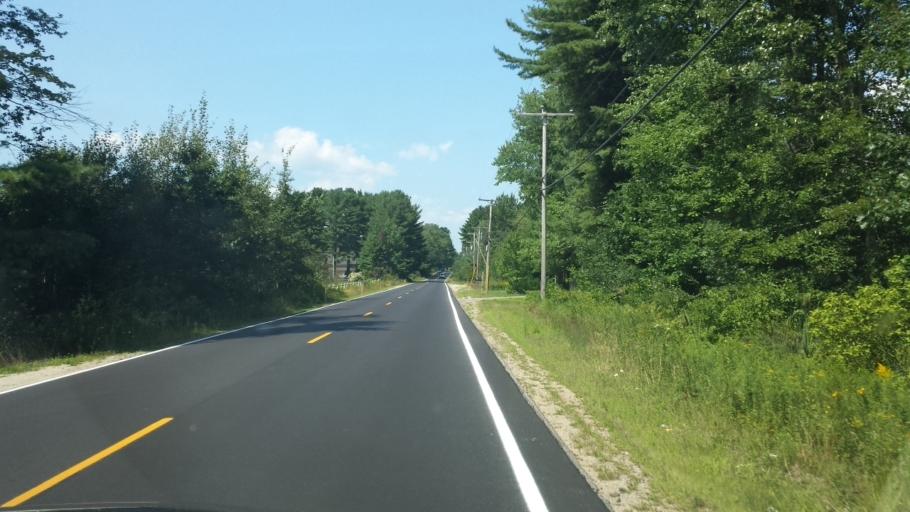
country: US
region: Maine
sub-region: York County
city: Arundel
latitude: 43.3997
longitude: -70.4860
